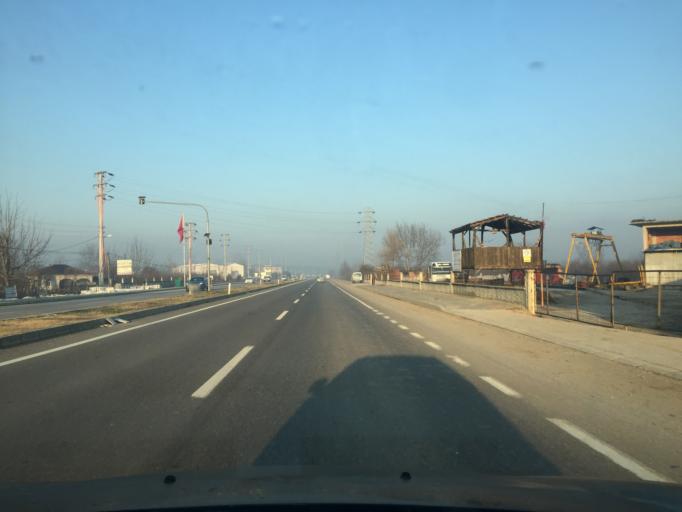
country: TR
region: Sakarya
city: Akyazi
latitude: 40.6362
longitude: 30.6243
